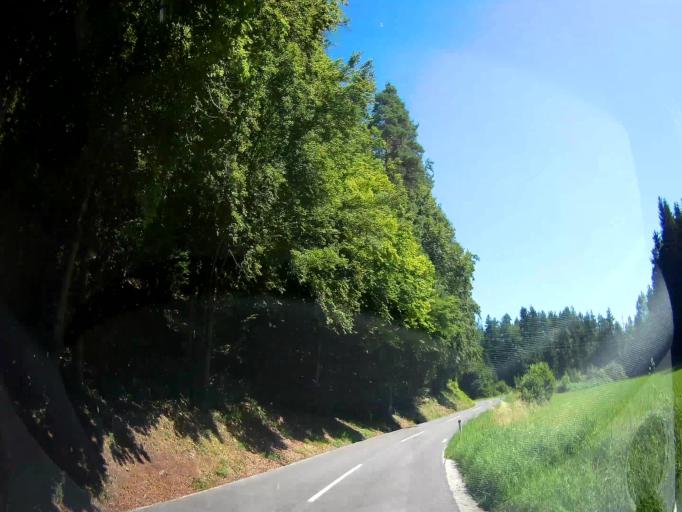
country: AT
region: Carinthia
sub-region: Politischer Bezirk Klagenfurt Land
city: Maria Worth
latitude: 46.5941
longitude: 14.1579
